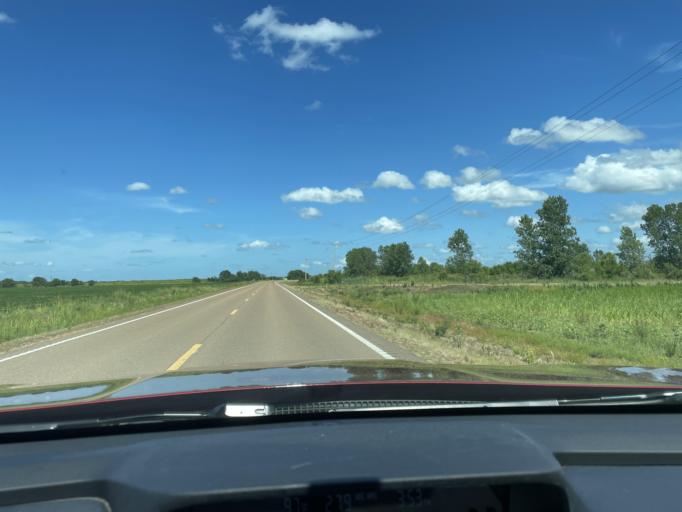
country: US
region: Mississippi
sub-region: Humphreys County
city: Belzoni
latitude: 33.1843
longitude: -90.6661
